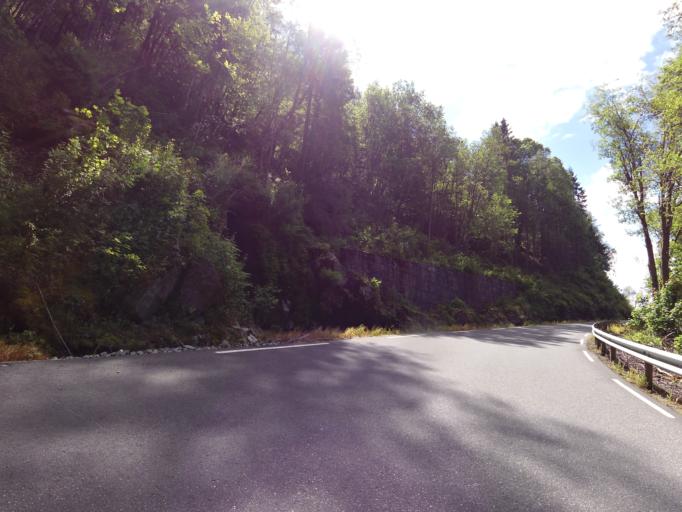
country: NO
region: Vest-Agder
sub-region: Kvinesdal
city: Liknes
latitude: 58.2932
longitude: 6.9437
